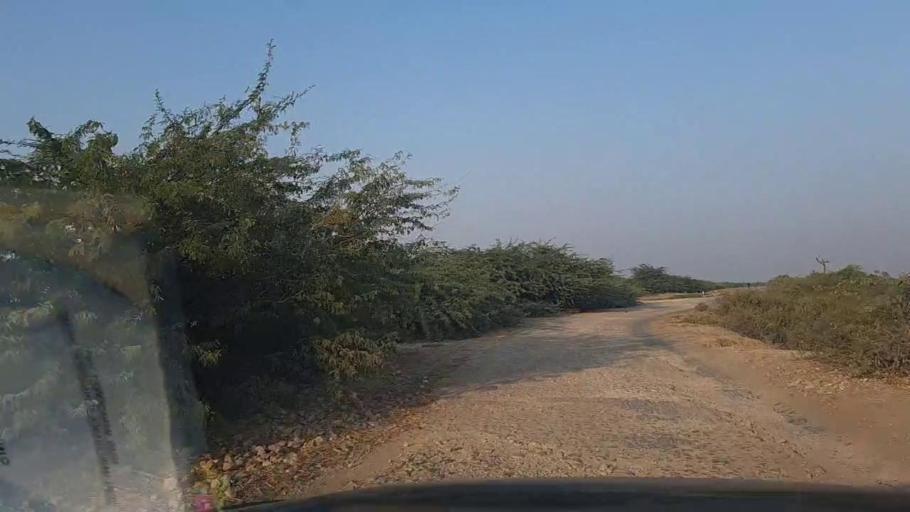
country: PK
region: Sindh
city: Keti Bandar
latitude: 24.2944
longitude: 67.5840
